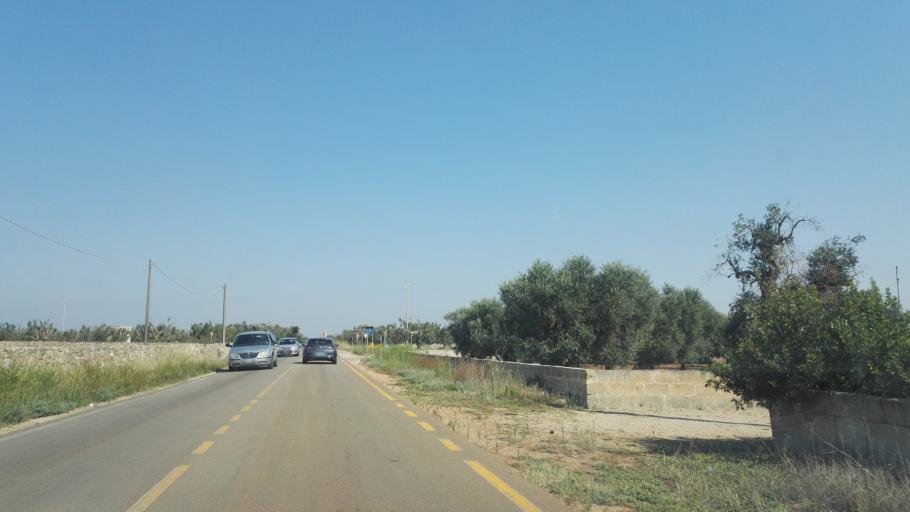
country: IT
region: Apulia
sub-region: Provincia di Lecce
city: Nardo
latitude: 40.1820
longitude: 17.9740
